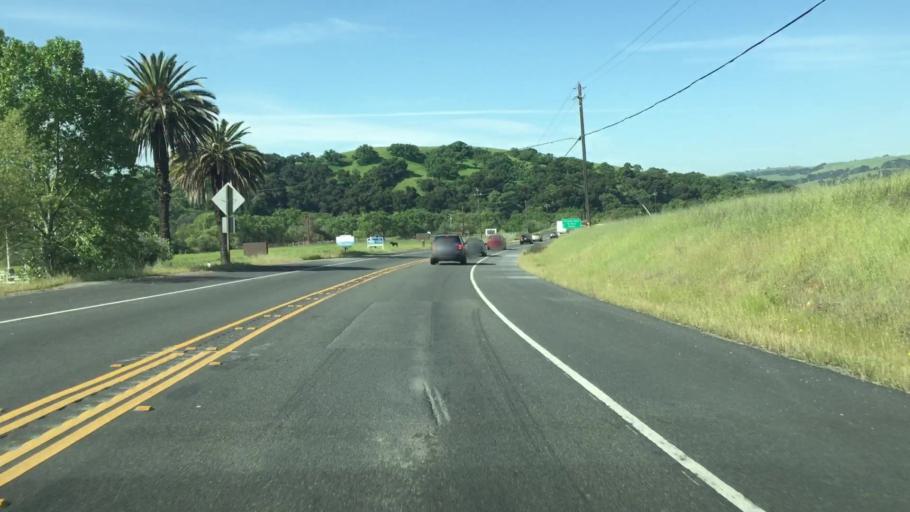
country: US
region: California
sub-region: Alameda County
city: Pleasanton
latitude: 37.6001
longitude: -121.8496
